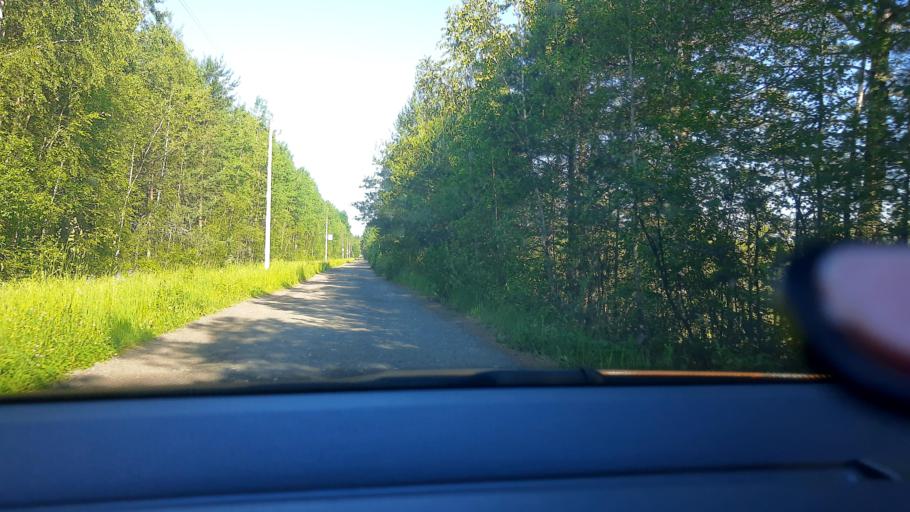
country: RU
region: Moskovskaya
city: Elektrogorsk
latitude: 55.8979
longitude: 38.7111
